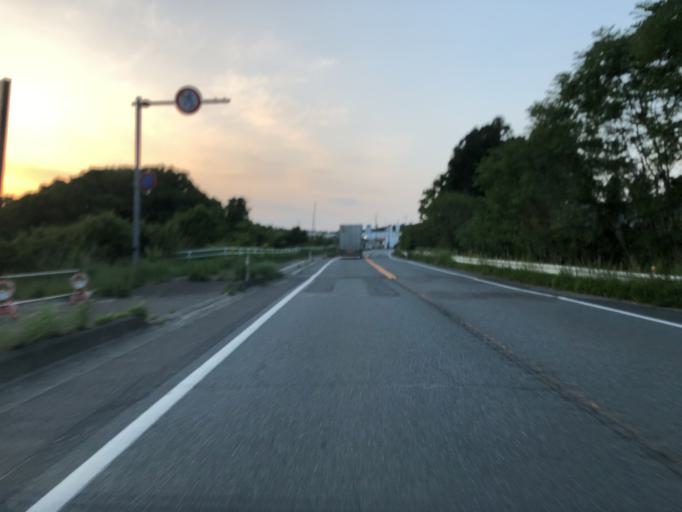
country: JP
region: Fukushima
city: Namie
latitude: 37.5022
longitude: 140.9988
